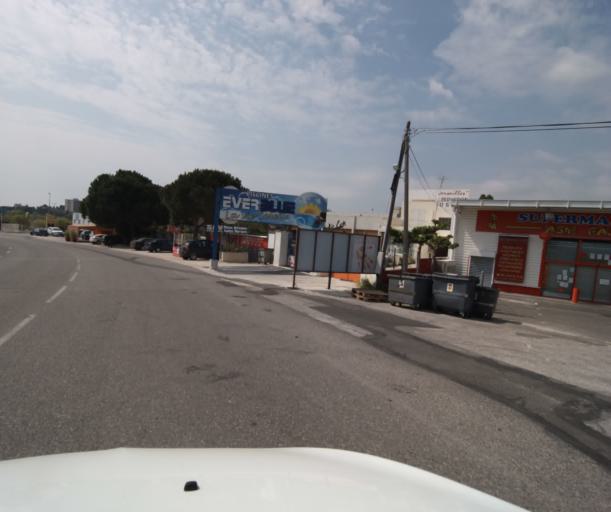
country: FR
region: Provence-Alpes-Cote d'Azur
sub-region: Departement du Var
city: La Garde
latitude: 43.1419
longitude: 6.0200
